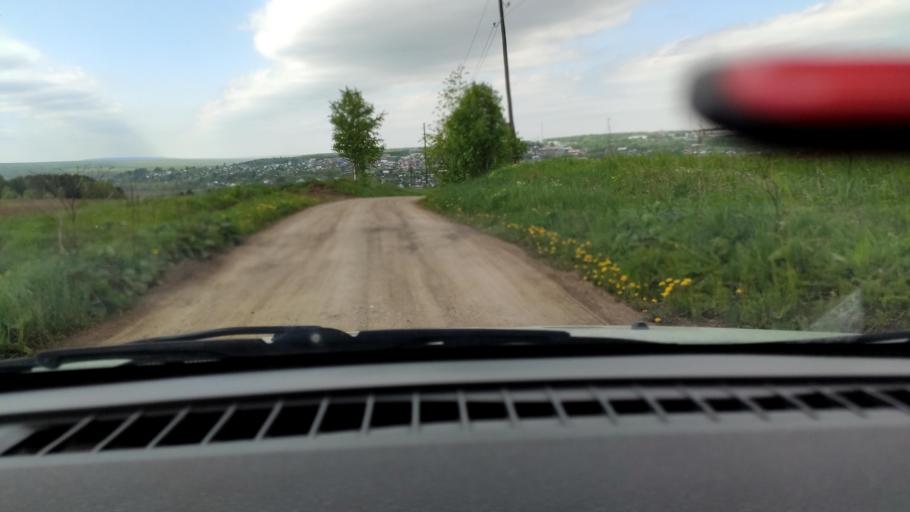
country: RU
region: Perm
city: Bershet'
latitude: 57.7242
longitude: 56.3930
